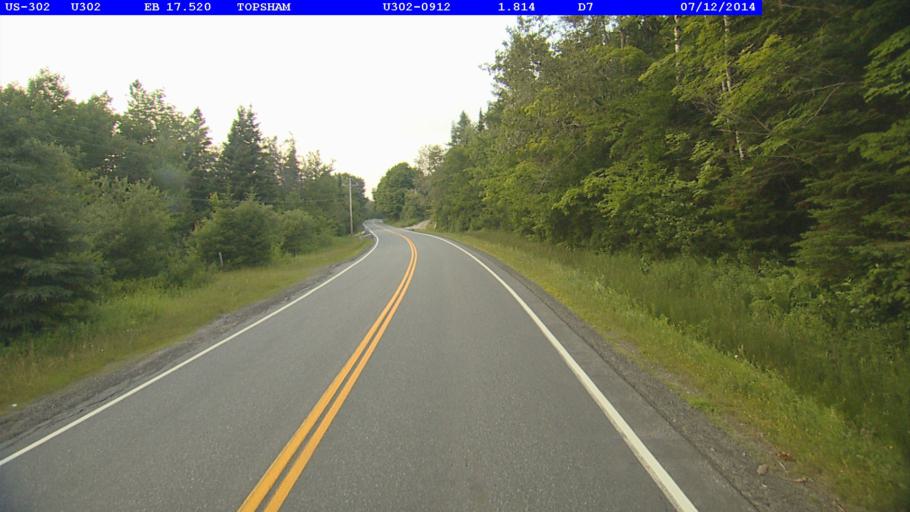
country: US
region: Vermont
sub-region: Washington County
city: Barre
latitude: 44.1622
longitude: -72.3066
